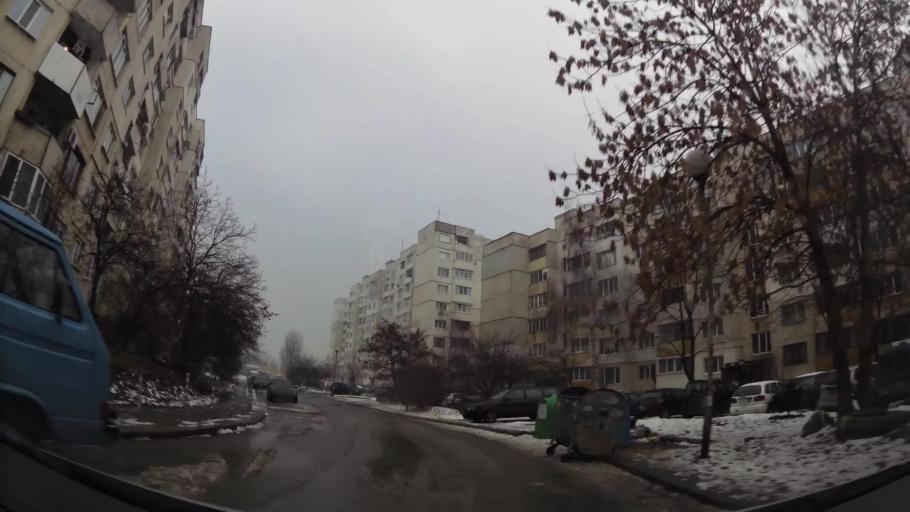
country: BG
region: Sofia-Capital
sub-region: Stolichna Obshtina
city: Sofia
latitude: 42.6894
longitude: 23.2585
